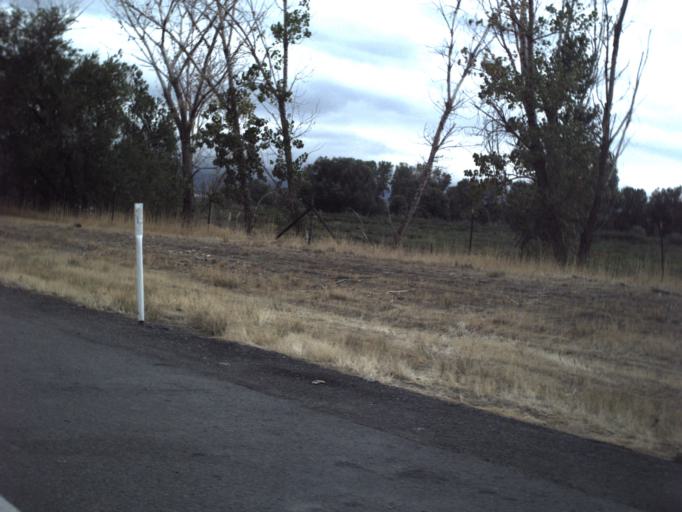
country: US
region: Utah
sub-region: Utah County
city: Springville
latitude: 40.1870
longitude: -111.6483
